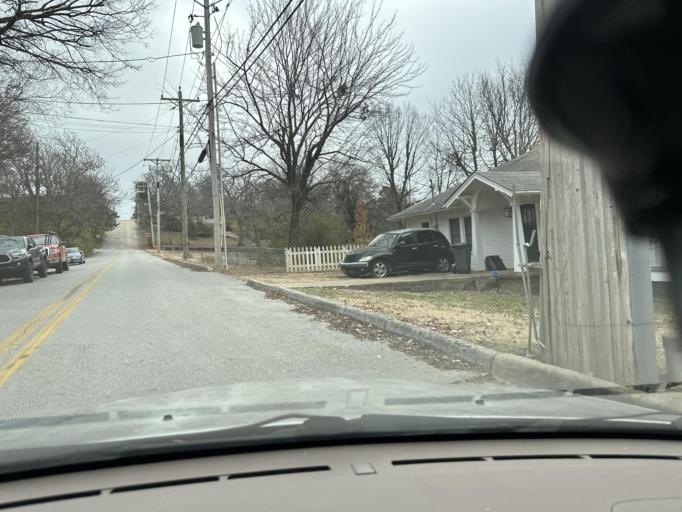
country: US
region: Arkansas
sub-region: Washington County
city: Fayetteville
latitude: 36.0610
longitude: -94.1643
